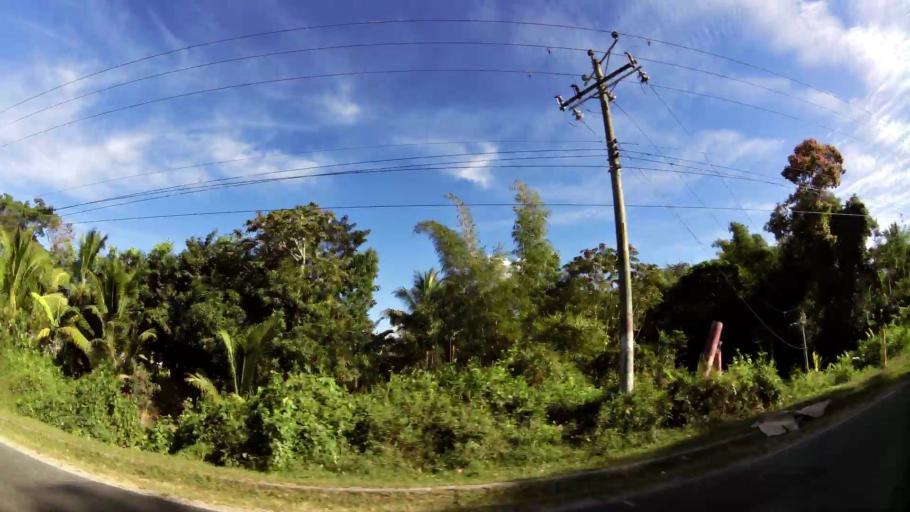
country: SV
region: Cuscatlan
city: Tecoluca
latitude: 13.7970
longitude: -89.0402
